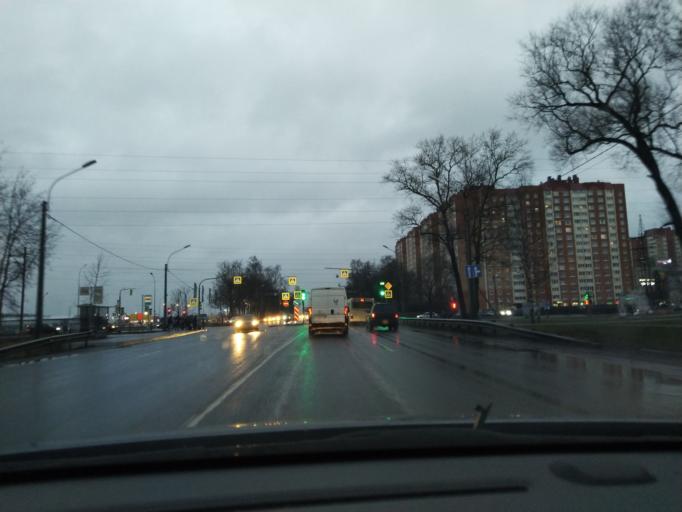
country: RU
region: St.-Petersburg
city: Gorelovo
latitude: 59.7904
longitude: 30.1454
